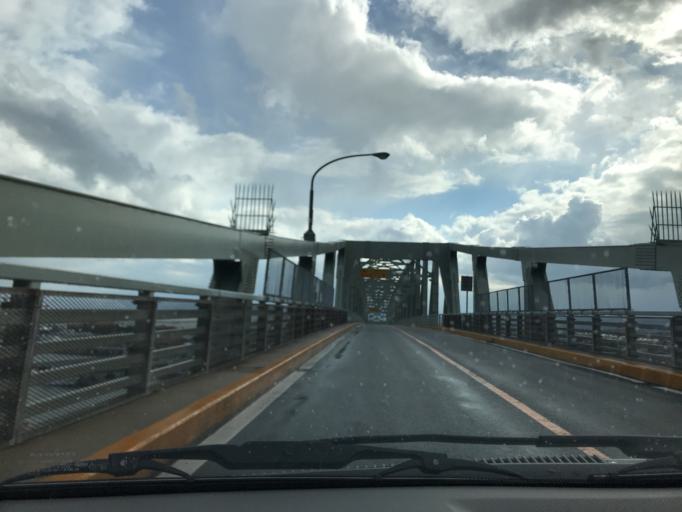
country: JP
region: Shimane
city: Sakaiminato
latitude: 35.5508
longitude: 133.2439
